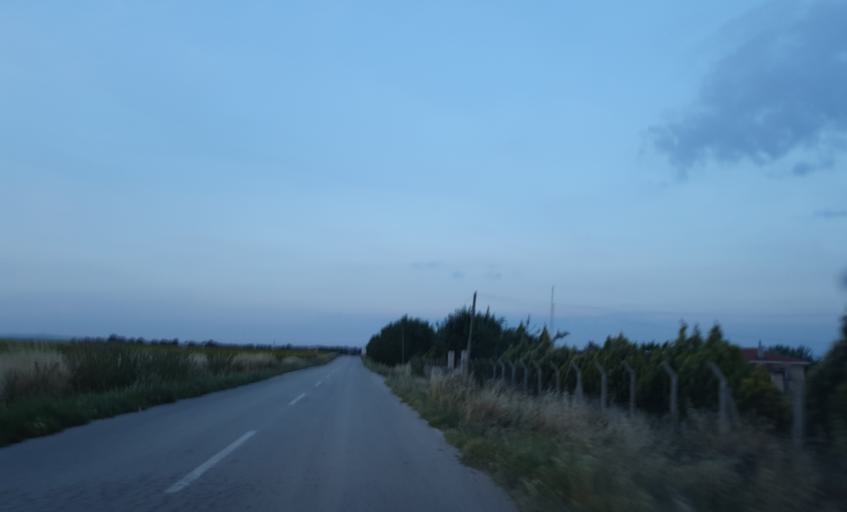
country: TR
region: Tekirdag
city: Beyazkoy
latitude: 41.4308
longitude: 27.6868
